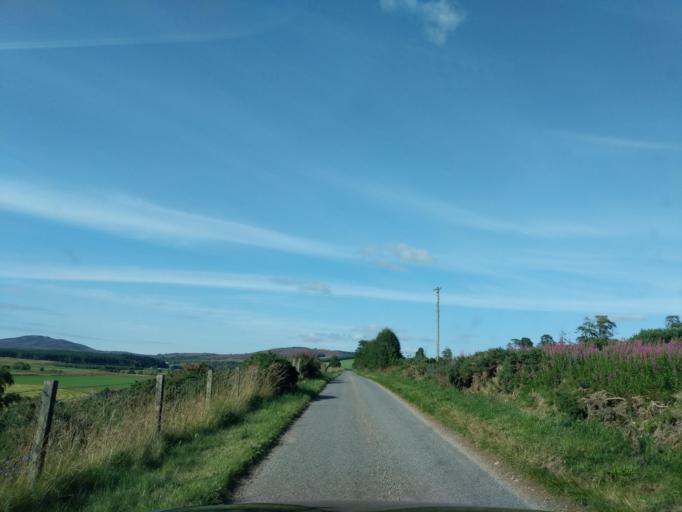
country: GB
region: Scotland
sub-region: Highland
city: Grantown on Spey
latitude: 57.2929
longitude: -3.7153
